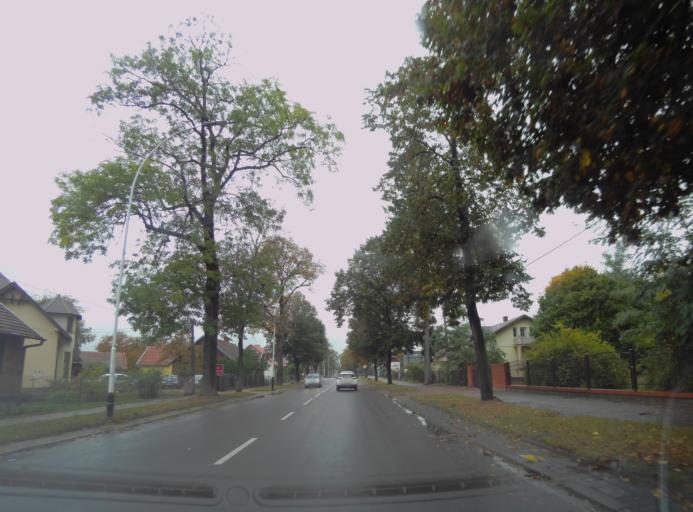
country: PL
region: Subcarpathian Voivodeship
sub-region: Powiat lezajski
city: Lezajsk
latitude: 50.2643
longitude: 22.4159
